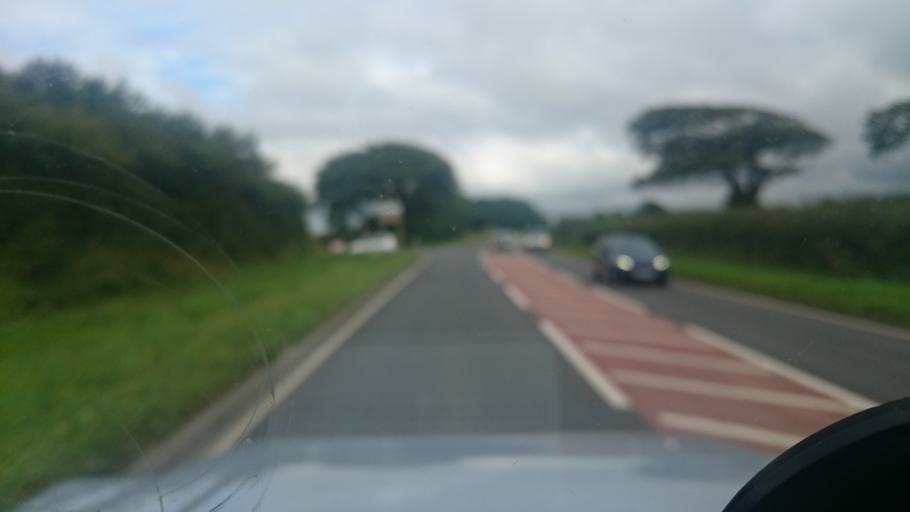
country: GB
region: Wales
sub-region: Pembrokeshire
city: Wiston
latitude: 51.8026
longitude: -4.8554
